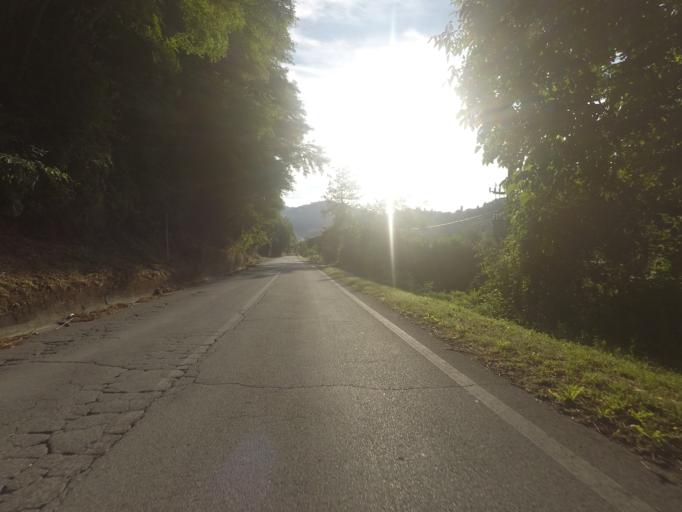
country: IT
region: Tuscany
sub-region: Provincia di Lucca
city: Pescaglia
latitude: 43.9524
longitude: 10.4388
